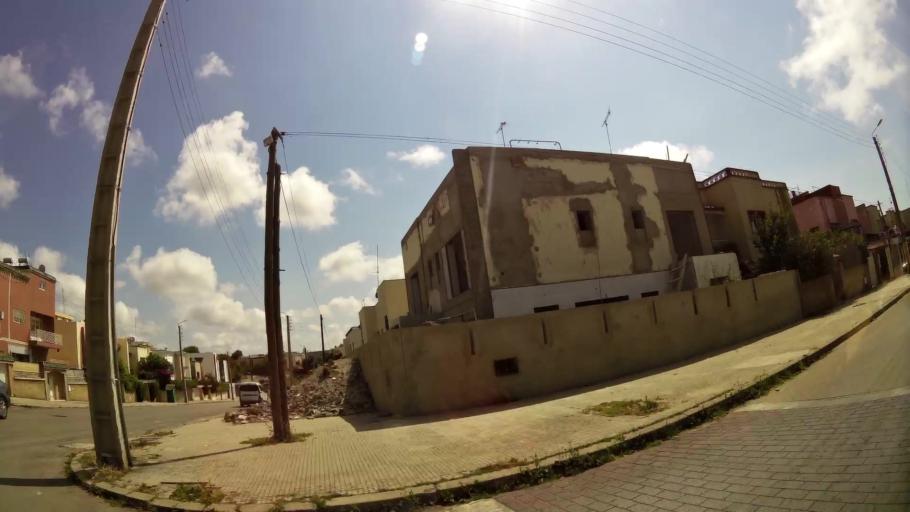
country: MA
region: Rabat-Sale-Zemmour-Zaer
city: Sale
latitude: 34.0387
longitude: -6.7901
